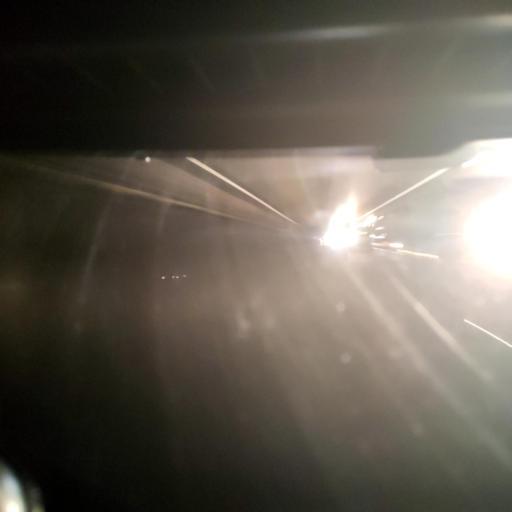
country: RU
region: Voronezj
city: Nizhnedevitsk
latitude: 51.6091
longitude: 38.6111
